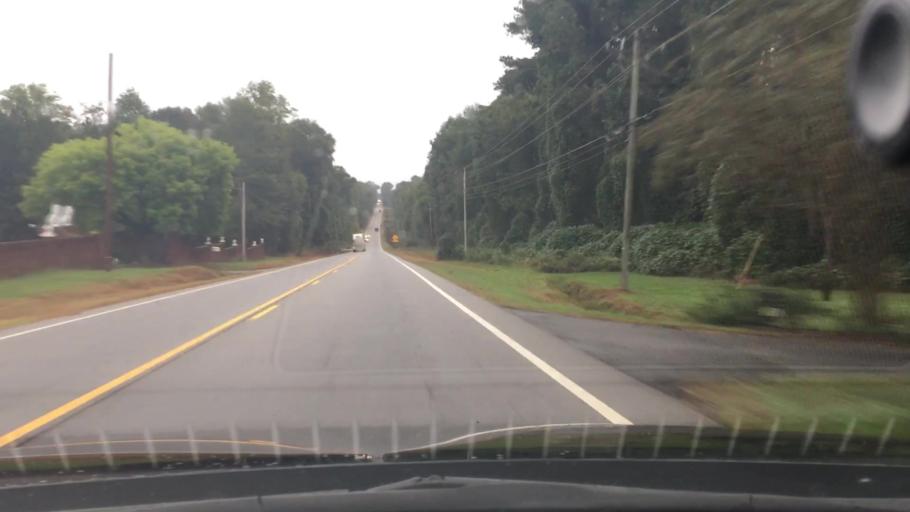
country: US
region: Georgia
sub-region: Spalding County
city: Experiment
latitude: 33.2409
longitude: -84.3689
